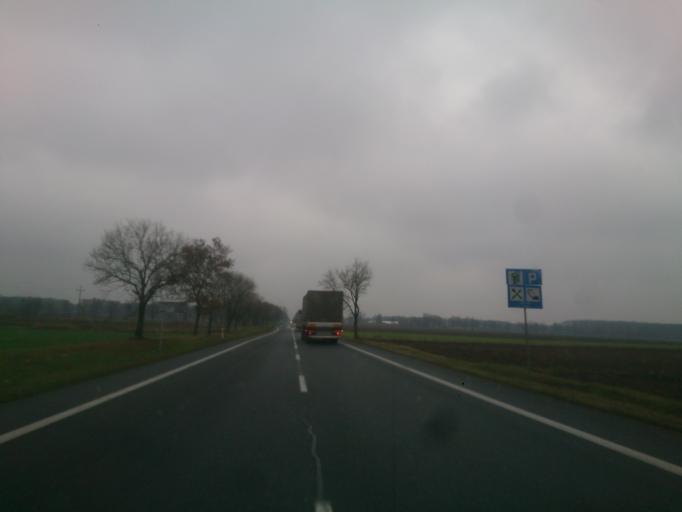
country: PL
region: Masovian Voivodeship
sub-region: Powiat sierpecki
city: Zawidz
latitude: 52.7925
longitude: 19.8748
